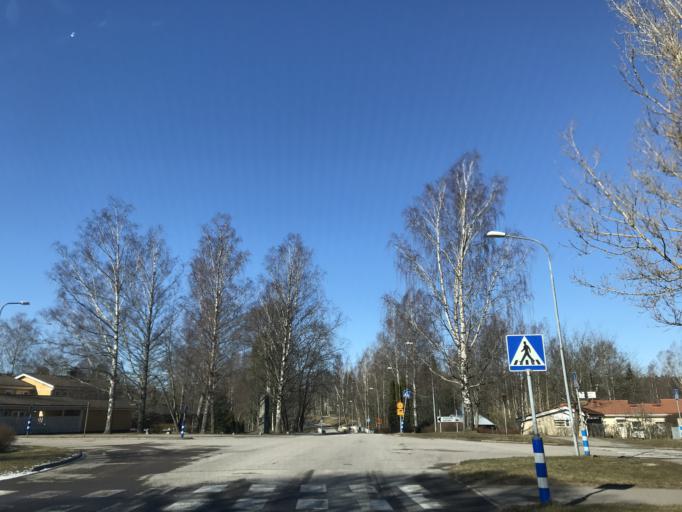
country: FI
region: Uusimaa
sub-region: Raaseporin
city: Karis
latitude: 60.0761
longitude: 23.6815
